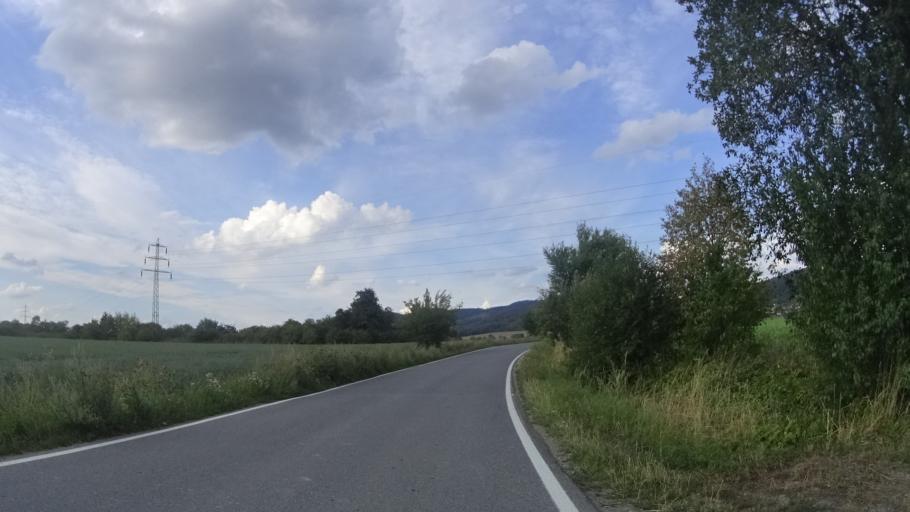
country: CZ
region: Olomoucky
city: Dubicko
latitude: 49.8388
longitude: 16.9378
